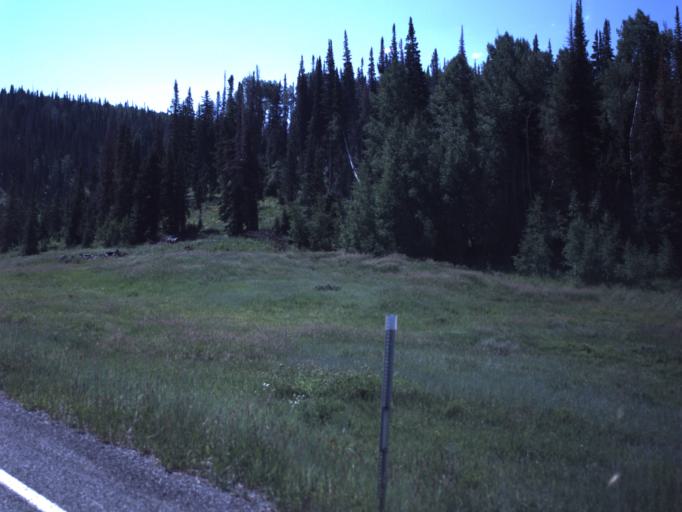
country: US
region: Utah
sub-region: Sanpete County
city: Fairview
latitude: 39.6517
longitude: -111.2881
